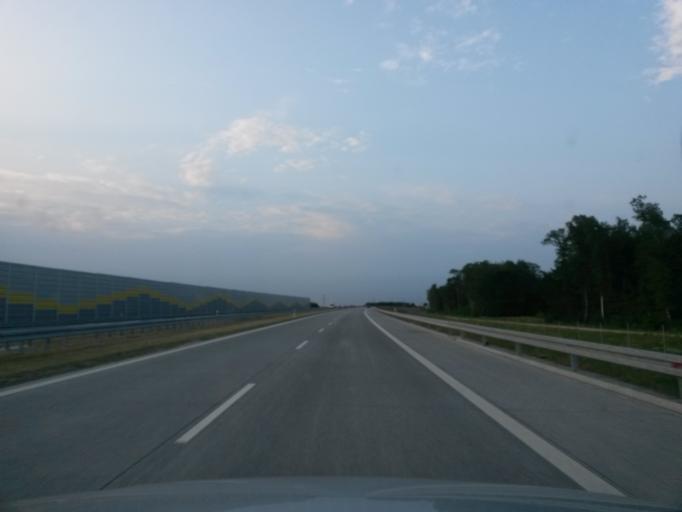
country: PL
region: Lodz Voivodeship
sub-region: Powiat sieradzki
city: Brzeznio
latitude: 51.4555
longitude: 18.6496
